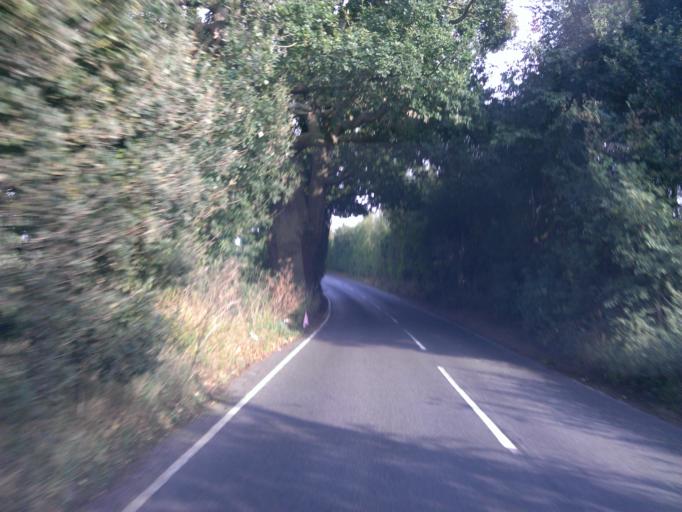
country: GB
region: England
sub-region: Essex
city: Witham
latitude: 51.8096
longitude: 0.6746
